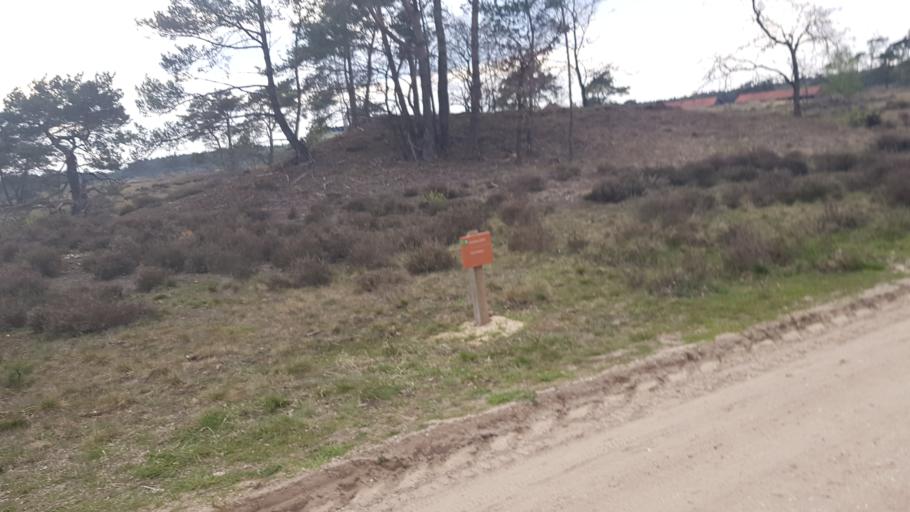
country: NL
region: Gelderland
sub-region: Gemeente Ede
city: Harskamp
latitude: 52.1715
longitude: 5.8248
